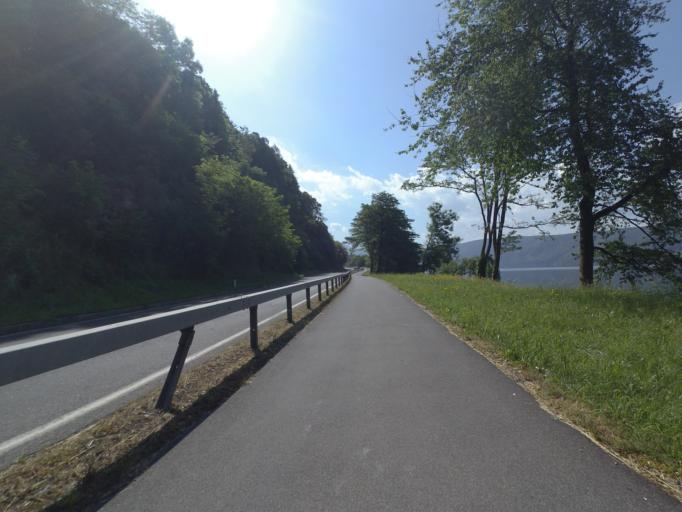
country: AT
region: Carinthia
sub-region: Politischer Bezirk Spittal an der Drau
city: Millstatt
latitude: 46.7926
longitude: 13.6066
